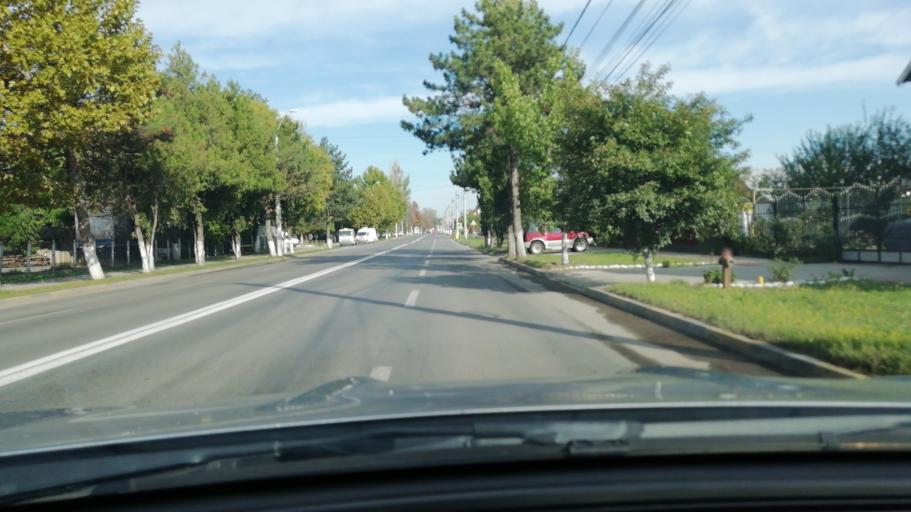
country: RO
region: Galati
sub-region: Municipiul Tecuci
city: Tecuci
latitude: 45.8225
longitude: 27.4387
